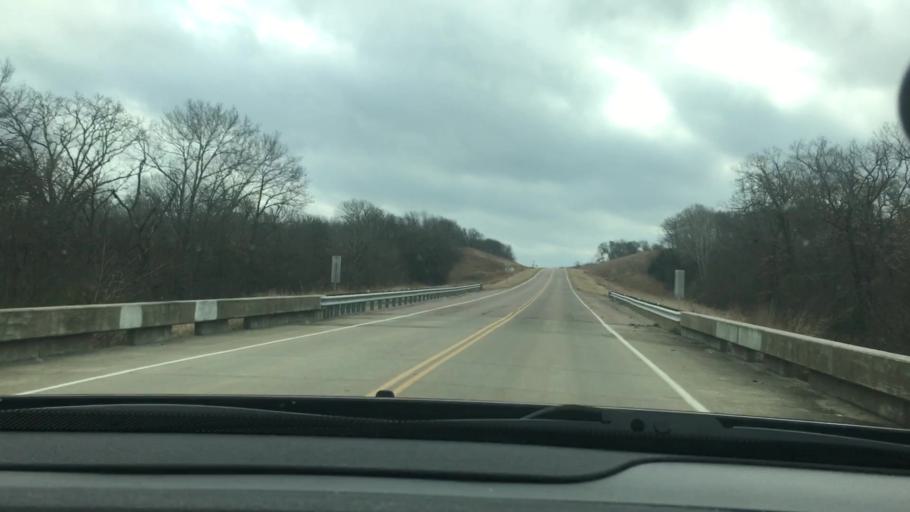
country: US
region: Oklahoma
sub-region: Bryan County
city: Durant
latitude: 34.0845
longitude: -96.3816
